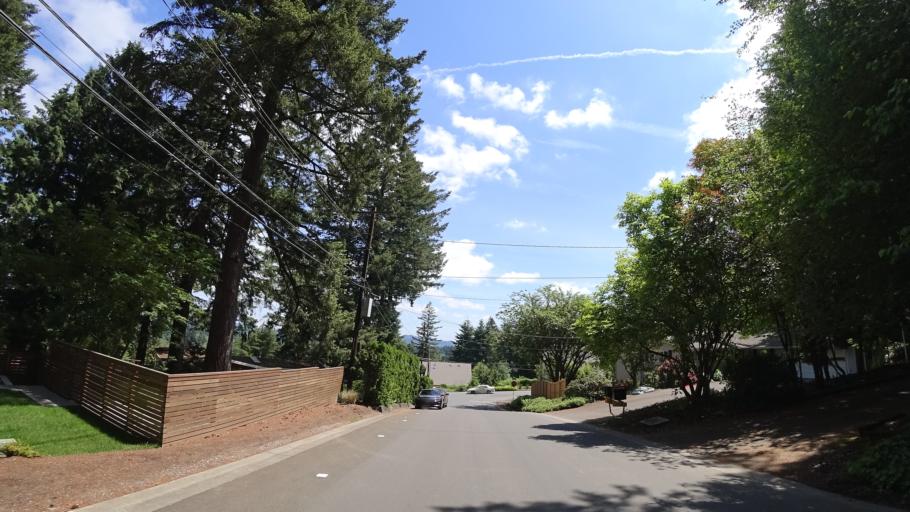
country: US
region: Oregon
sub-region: Washington County
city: King City
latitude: 45.4277
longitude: -122.8167
